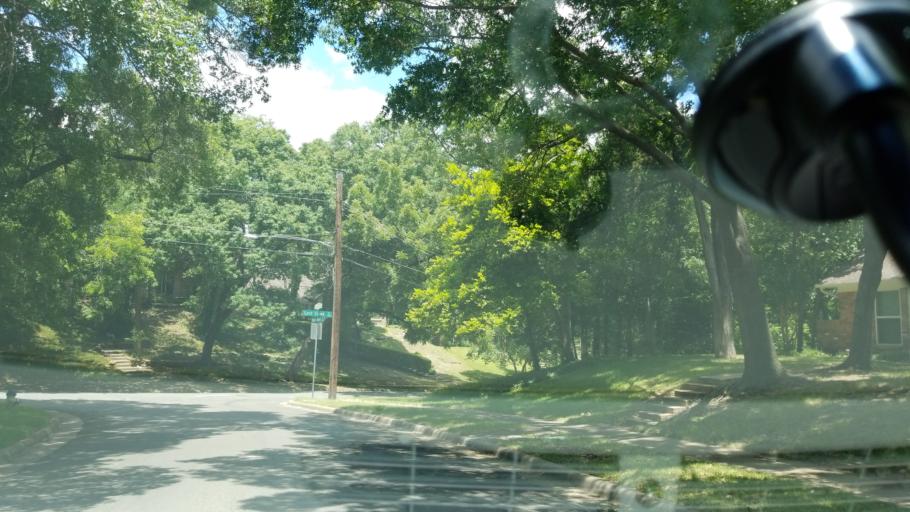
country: US
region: Texas
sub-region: Dallas County
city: Cockrell Hill
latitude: 32.6943
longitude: -96.8474
